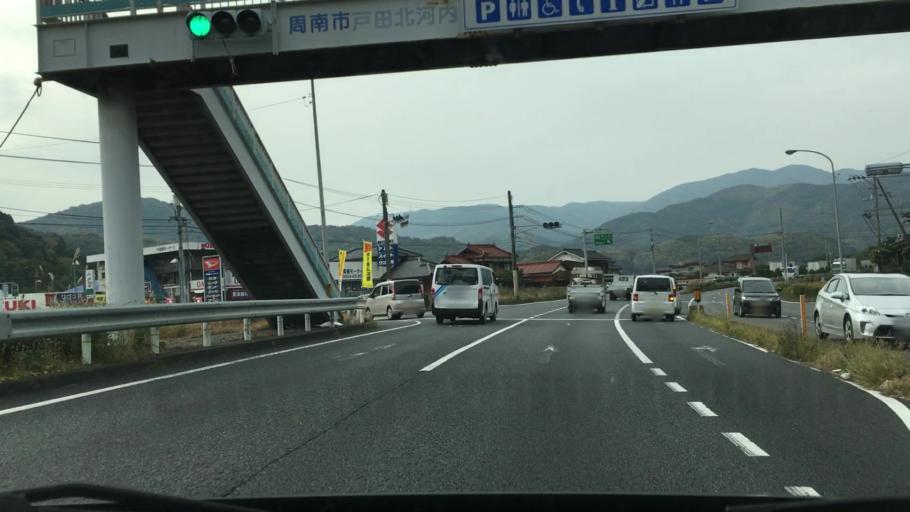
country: JP
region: Yamaguchi
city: Tokuyama
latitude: 34.0691
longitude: 131.6982
